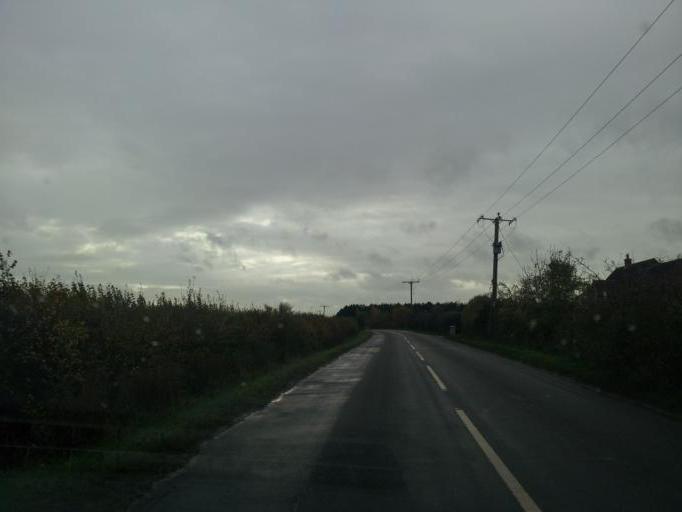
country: GB
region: England
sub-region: Nottinghamshire
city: Newark on Trent
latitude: 53.0305
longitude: -0.8011
